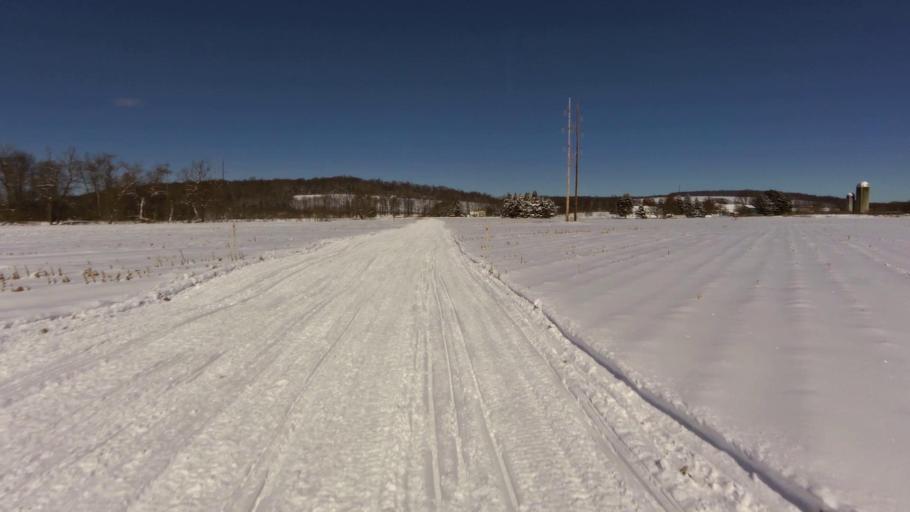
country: US
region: New York
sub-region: Chautauqua County
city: Celoron
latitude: 42.2418
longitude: -79.2829
